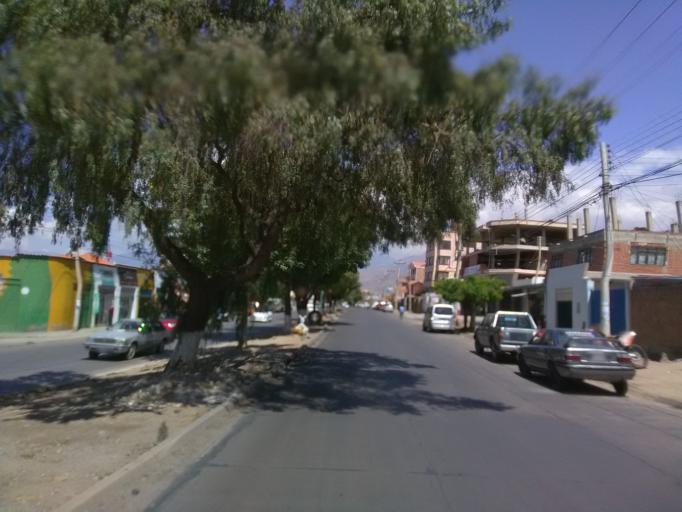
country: BO
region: Cochabamba
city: Cochabamba
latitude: -17.3588
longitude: -66.1738
